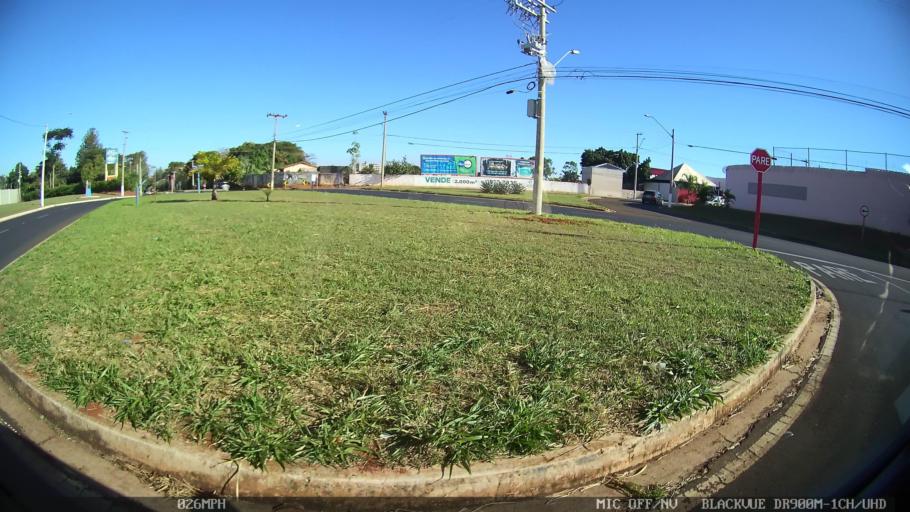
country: BR
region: Sao Paulo
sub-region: Araraquara
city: Araraquara
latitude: -21.7485
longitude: -48.1836
